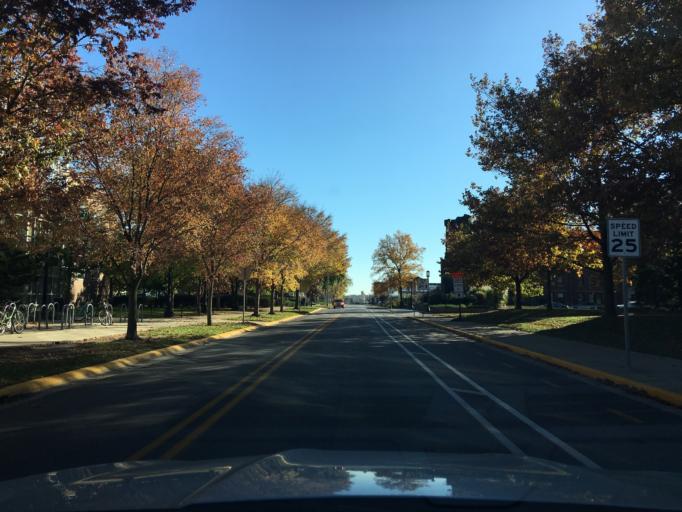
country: US
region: Indiana
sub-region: Tippecanoe County
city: West Lafayette
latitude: 40.4229
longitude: -86.9138
